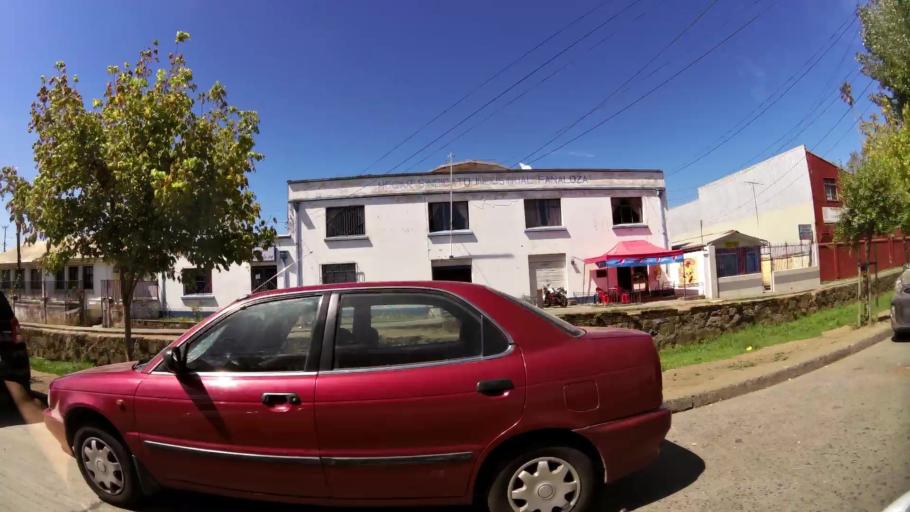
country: CL
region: Biobio
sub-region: Provincia de Concepcion
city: Penco
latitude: -36.7379
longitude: -72.9950
